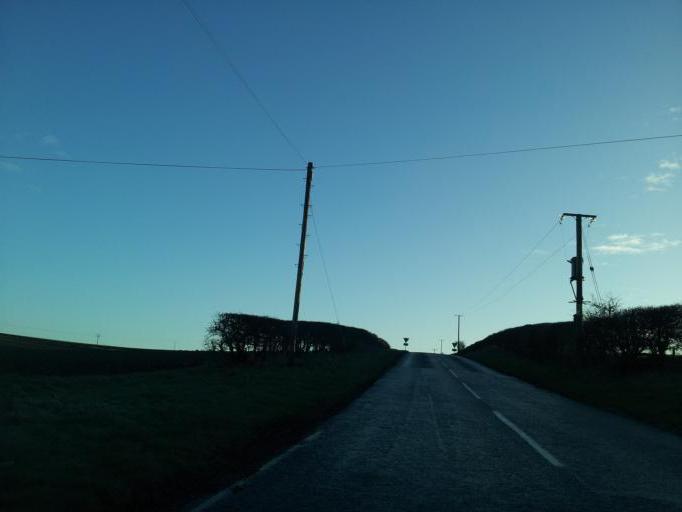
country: GB
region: England
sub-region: Lincolnshire
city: Horncastle
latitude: 53.2597
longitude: -0.0902
